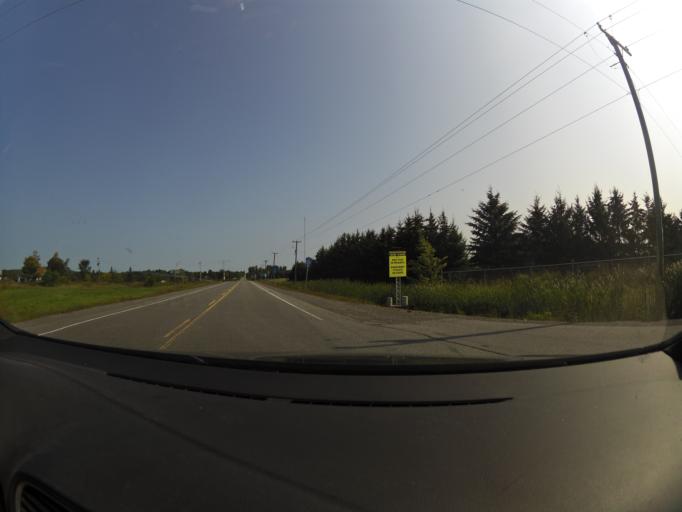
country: CA
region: Ontario
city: Arnprior
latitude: 45.4577
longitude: -76.2014
